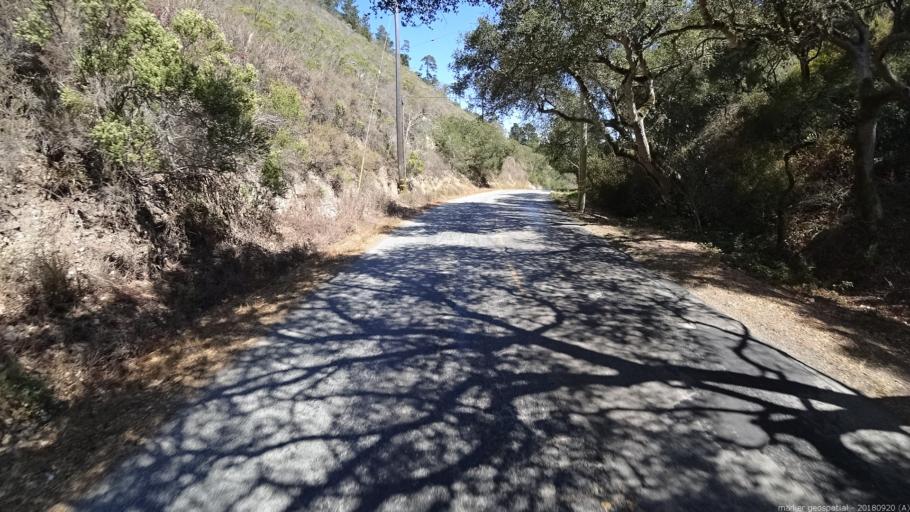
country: US
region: California
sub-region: Monterey County
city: Monterey
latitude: 36.5729
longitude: -121.8828
